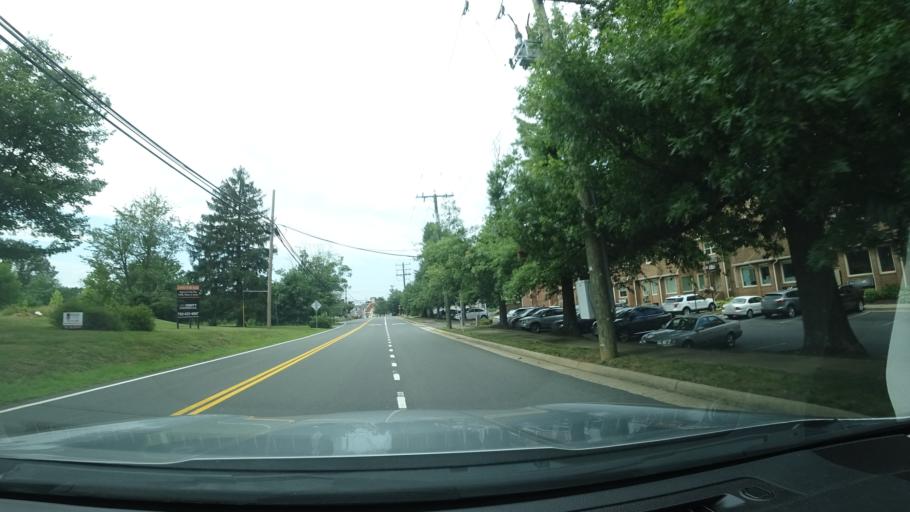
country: US
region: Virginia
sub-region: Fairfax County
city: Great Falls
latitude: 38.9748
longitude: -77.2958
